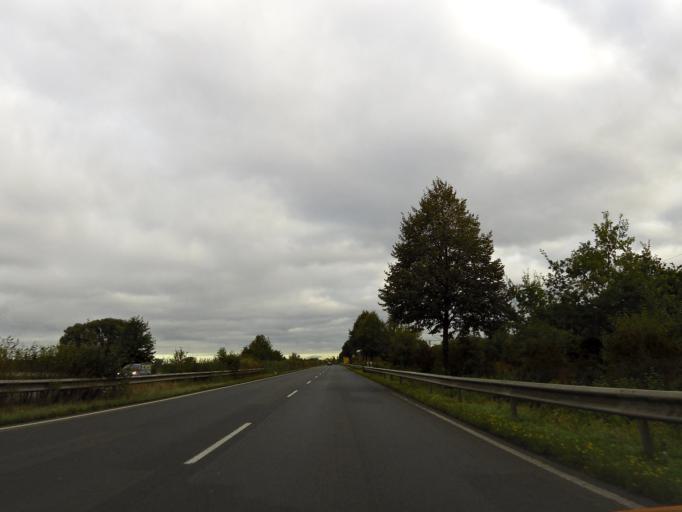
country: DE
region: Lower Saxony
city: Bovenden
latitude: 51.5741
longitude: 9.9218
